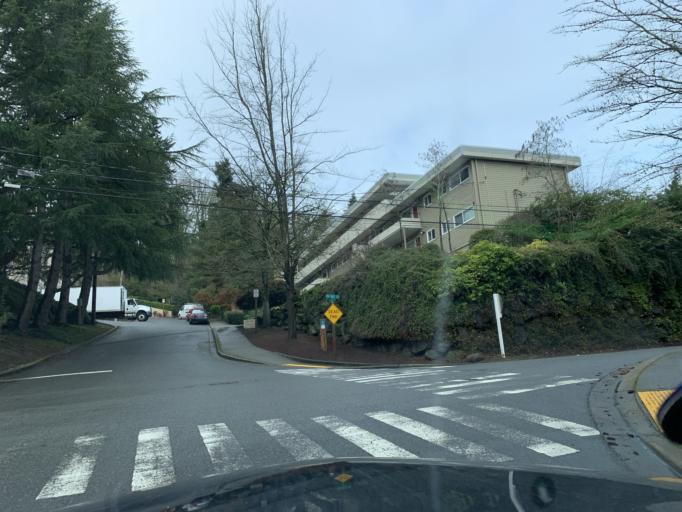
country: US
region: Washington
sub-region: King County
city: Mercer Island
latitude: 47.5844
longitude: -122.2375
